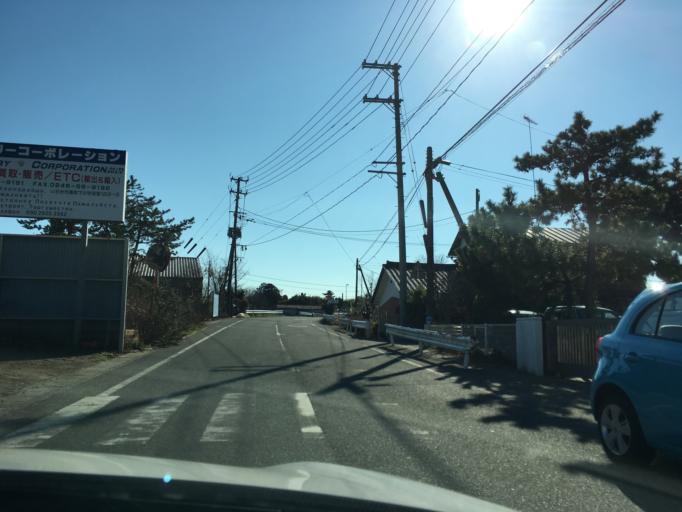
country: JP
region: Fukushima
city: Iwaki
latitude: 36.9365
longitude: 140.8643
